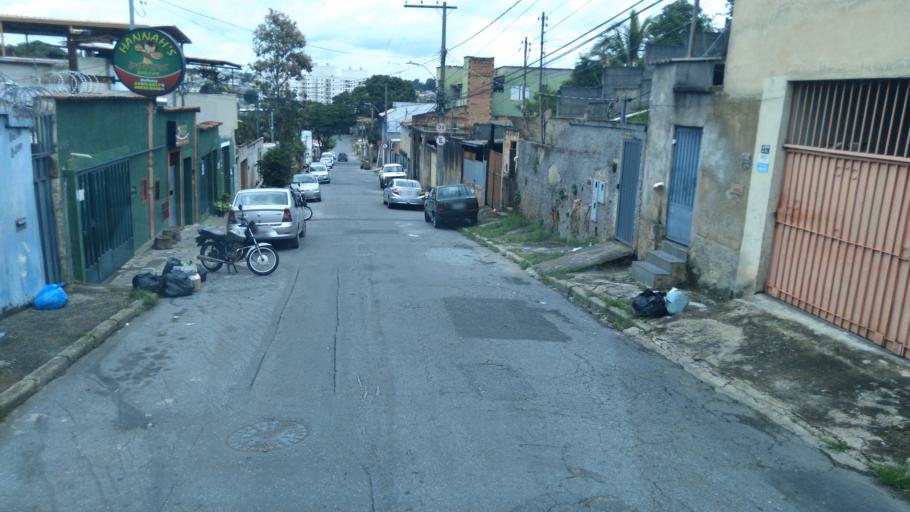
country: BR
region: Minas Gerais
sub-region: Belo Horizonte
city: Belo Horizonte
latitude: -19.9107
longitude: -43.8979
